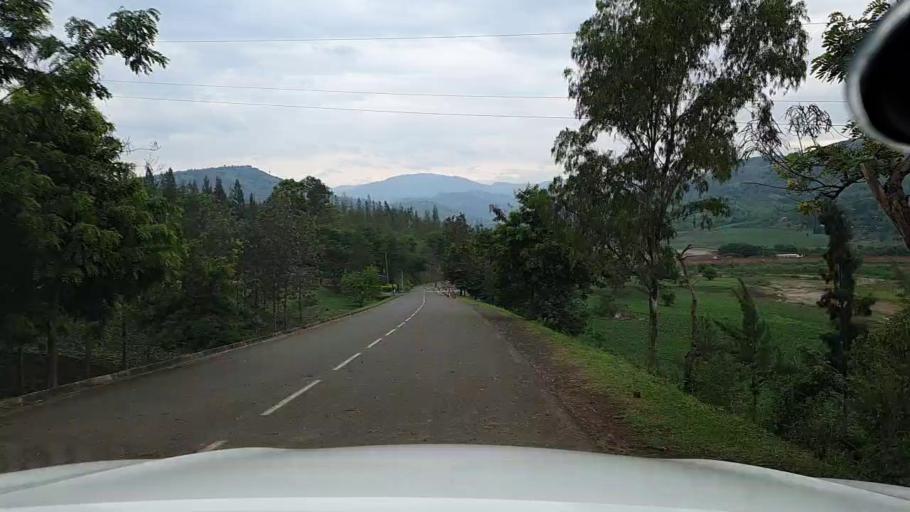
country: BI
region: Cibitoke
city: Cibitoke
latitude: -2.7333
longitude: 29.0389
